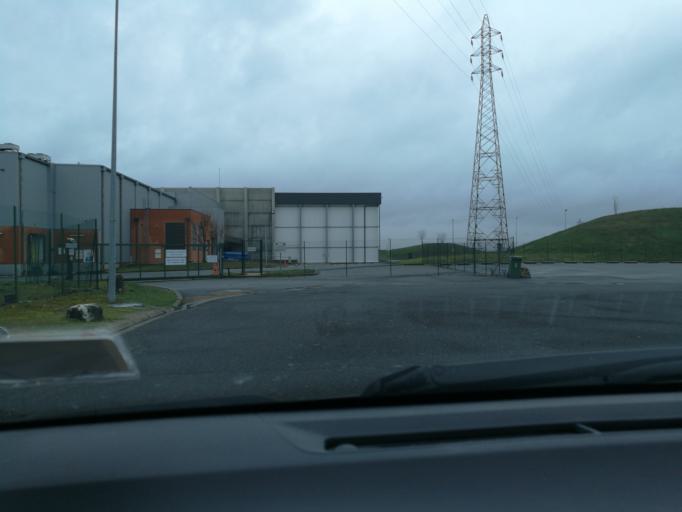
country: FR
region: Centre
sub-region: Departement du Loiret
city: Fleury-les-Aubrais
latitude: 47.9449
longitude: 1.9311
